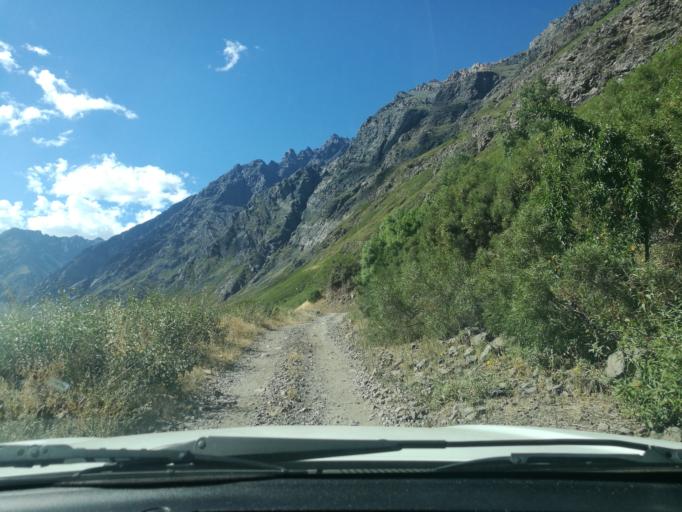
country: CL
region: O'Higgins
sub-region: Provincia de Cachapoal
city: Machali
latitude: -34.3852
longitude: -70.2824
